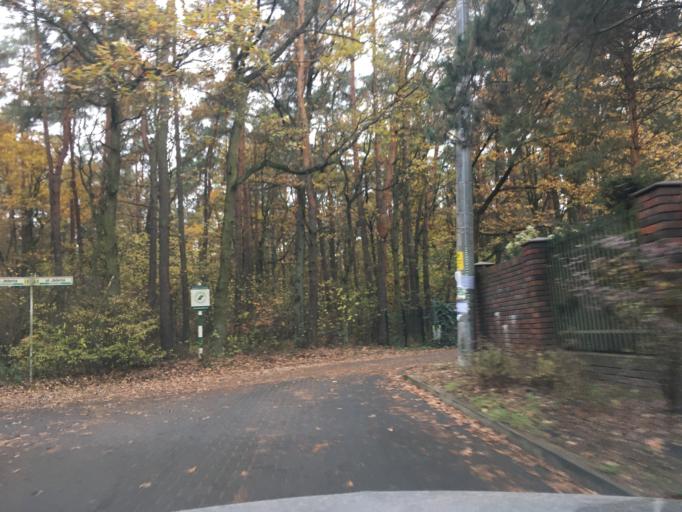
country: PL
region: Masovian Voivodeship
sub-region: Powiat piaseczynski
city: Lesznowola
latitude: 52.0750
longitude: 20.9178
